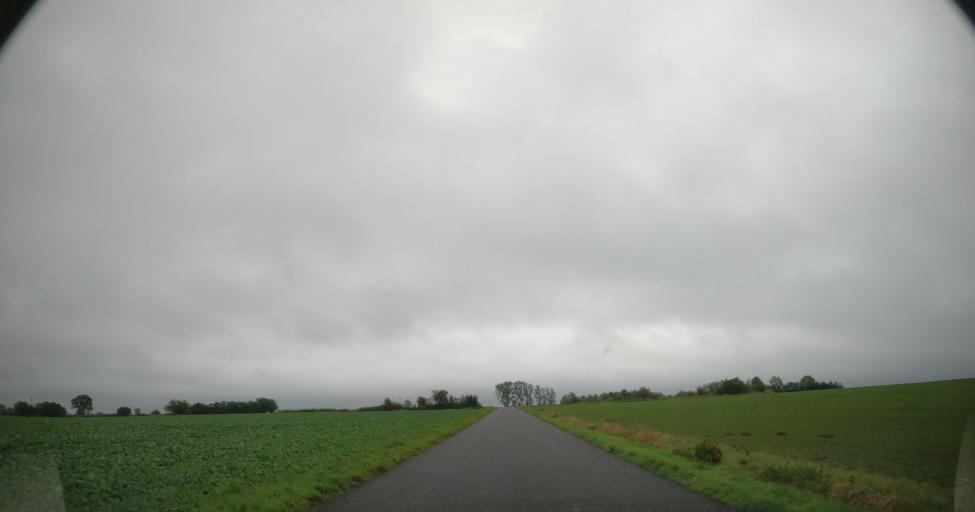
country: PL
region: West Pomeranian Voivodeship
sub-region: Powiat pyrzycki
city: Kozielice
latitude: 53.1199
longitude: 14.7567
